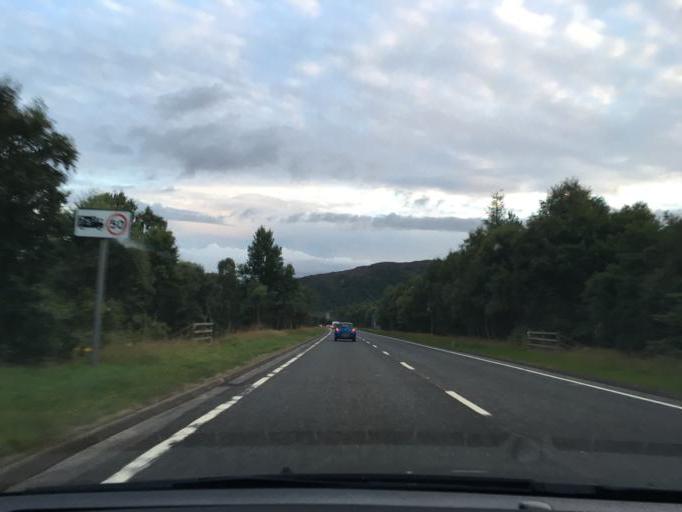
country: GB
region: Scotland
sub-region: Highland
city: Aviemore
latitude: 57.2024
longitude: -3.8332
